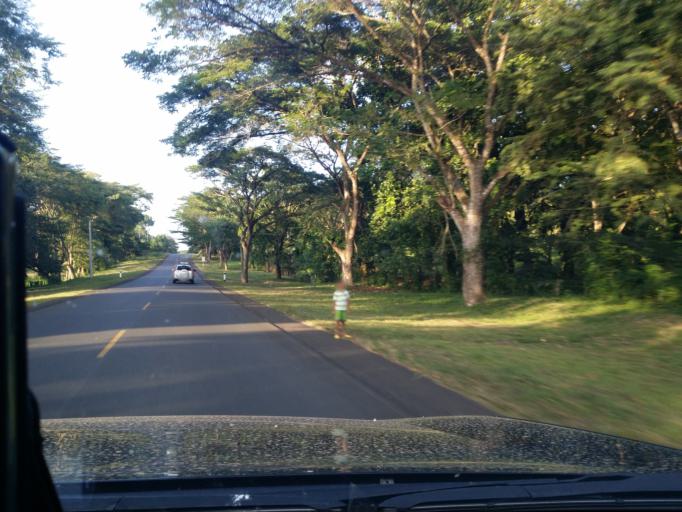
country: NI
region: Rio San Juan
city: San Miguelito
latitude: 11.4708
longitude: -84.8471
